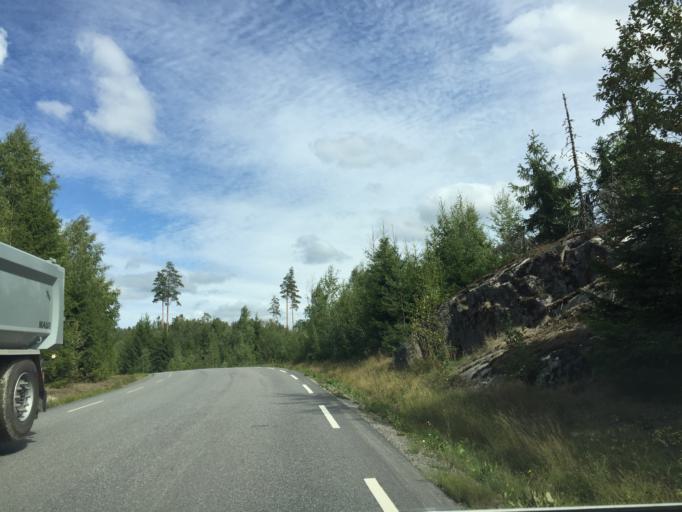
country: NO
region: Ostfold
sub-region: Hobol
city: Elvestad
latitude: 59.6067
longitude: 10.9029
